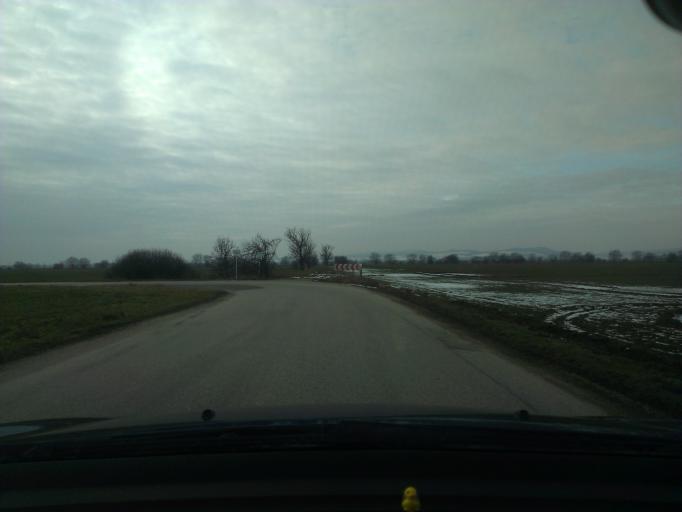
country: SK
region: Trnavsky
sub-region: Okres Trnava
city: Piestany
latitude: 48.6010
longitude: 17.8104
